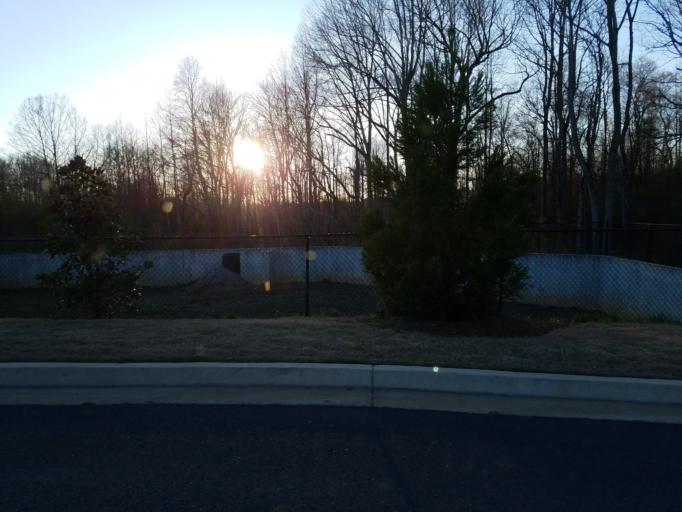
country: US
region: Georgia
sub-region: Dawson County
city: Dawsonville
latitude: 34.3574
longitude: -84.0348
